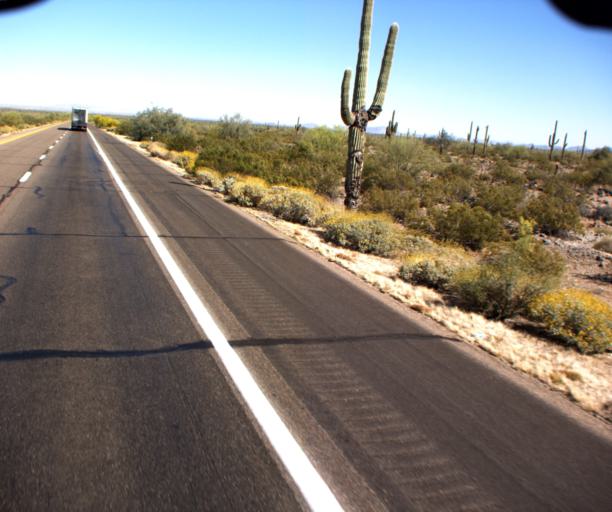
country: US
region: Arizona
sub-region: Pinal County
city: Maricopa
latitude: 32.8313
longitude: -112.0566
